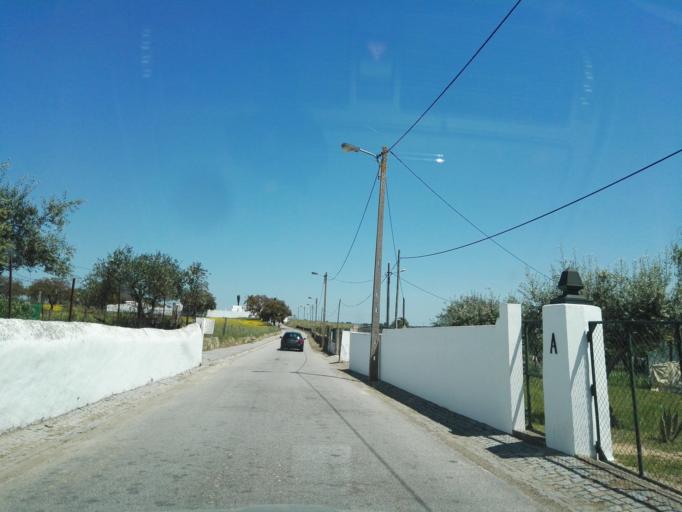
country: PT
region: Portalegre
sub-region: Arronches
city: Arronches
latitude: 39.0078
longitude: -7.2459
